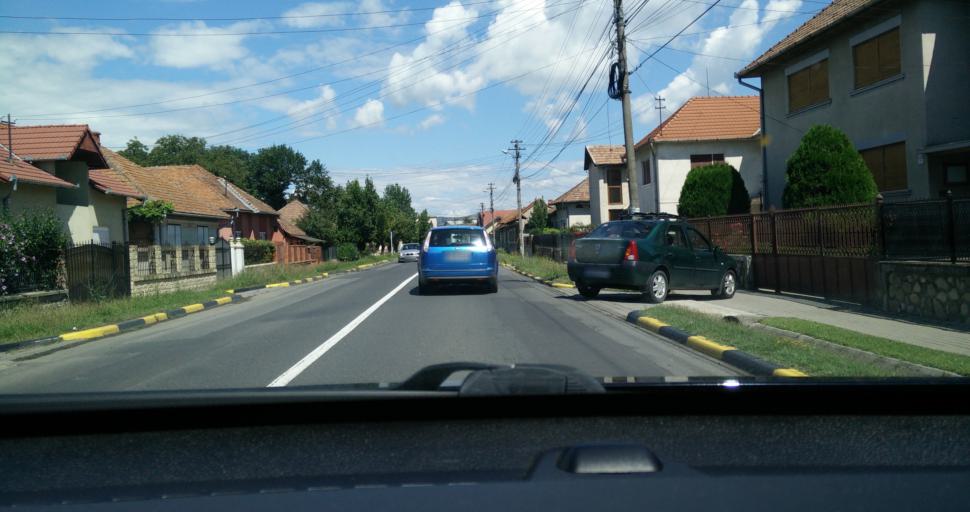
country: RO
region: Alba
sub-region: Municipiul Sebes
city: Sebes
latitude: 45.9473
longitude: 23.5648
